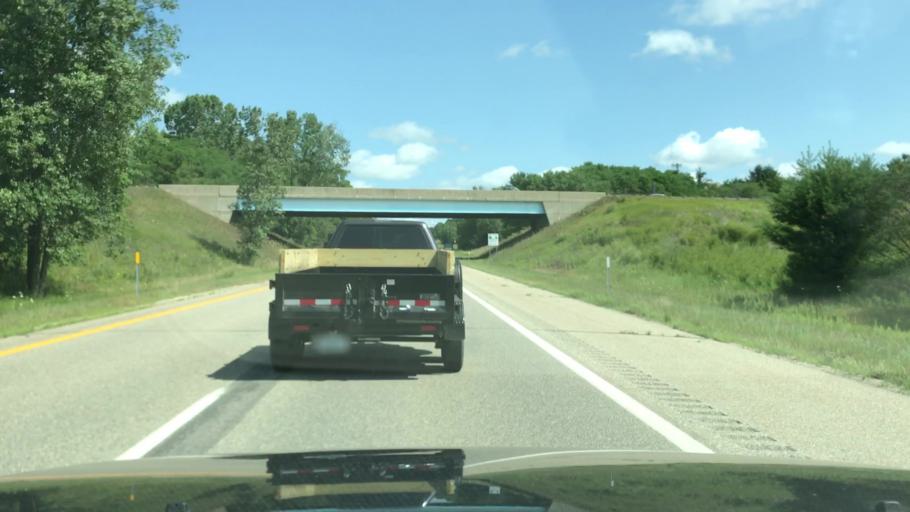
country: US
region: Michigan
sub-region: Mecosta County
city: Big Rapids
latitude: 43.7417
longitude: -85.5307
